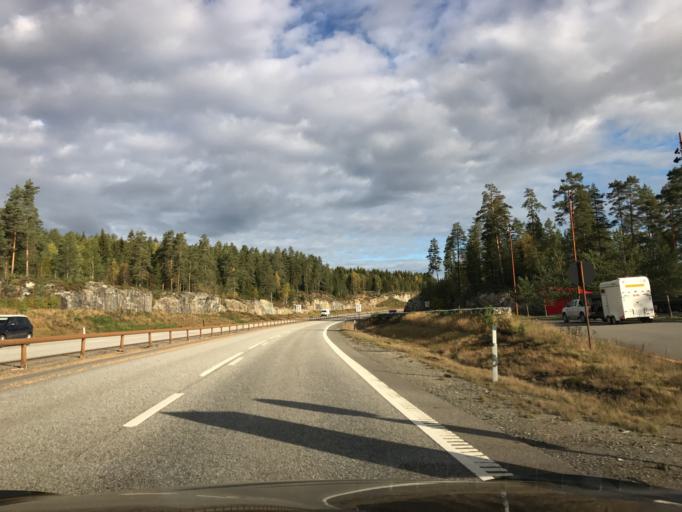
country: NO
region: Akershus
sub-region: Eidsvoll
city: Raholt
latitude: 60.2882
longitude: 11.1338
